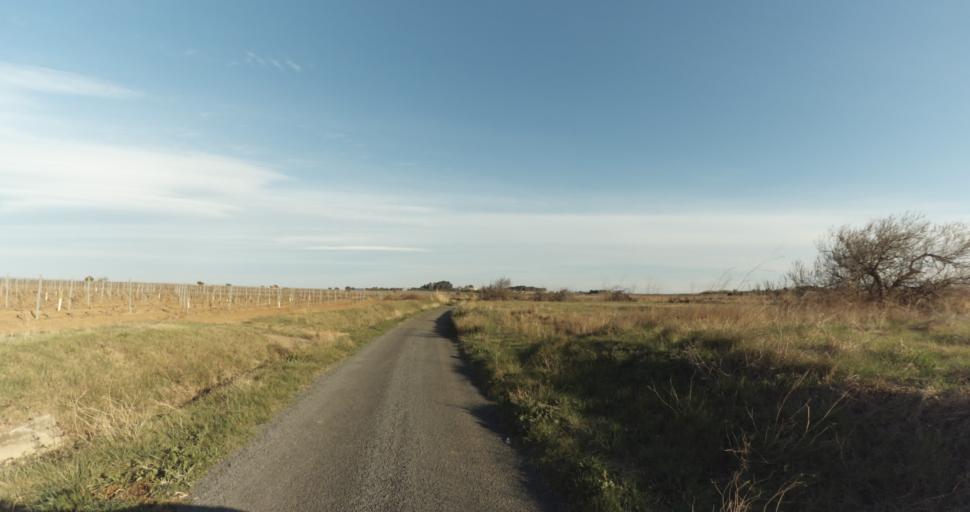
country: FR
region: Languedoc-Roussillon
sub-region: Departement de l'Herault
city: Marseillan
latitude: 43.3738
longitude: 3.5257
